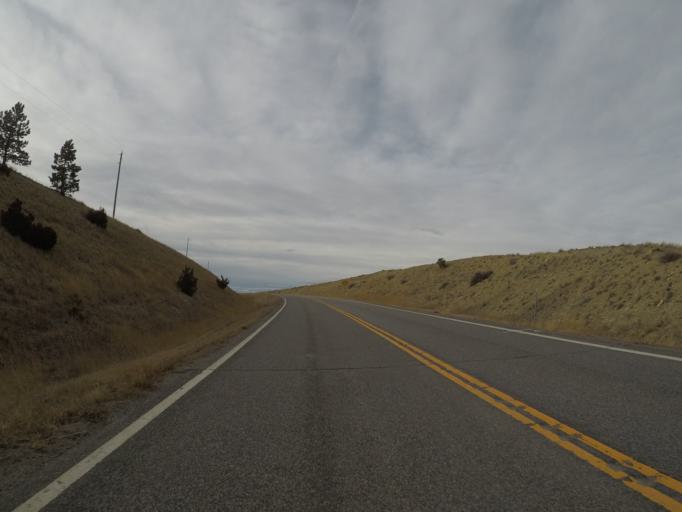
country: US
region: Montana
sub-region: Yellowstone County
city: Laurel
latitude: 45.8562
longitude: -108.7631
